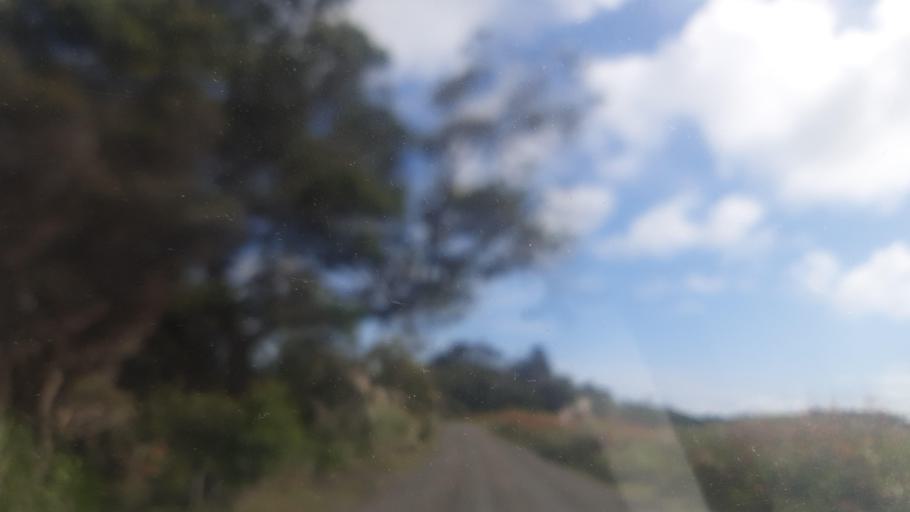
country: NZ
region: Northland
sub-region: Far North District
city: Kaitaia
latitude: -34.7595
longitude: 173.0481
